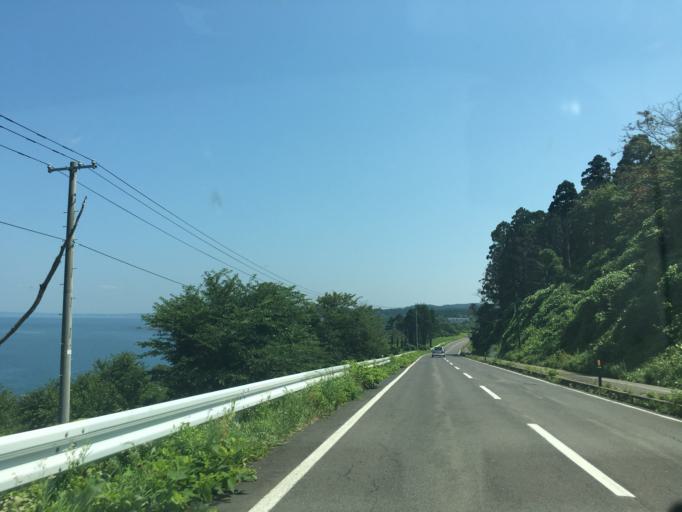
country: JP
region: Akita
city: Tenno
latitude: 39.9868
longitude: 139.7160
